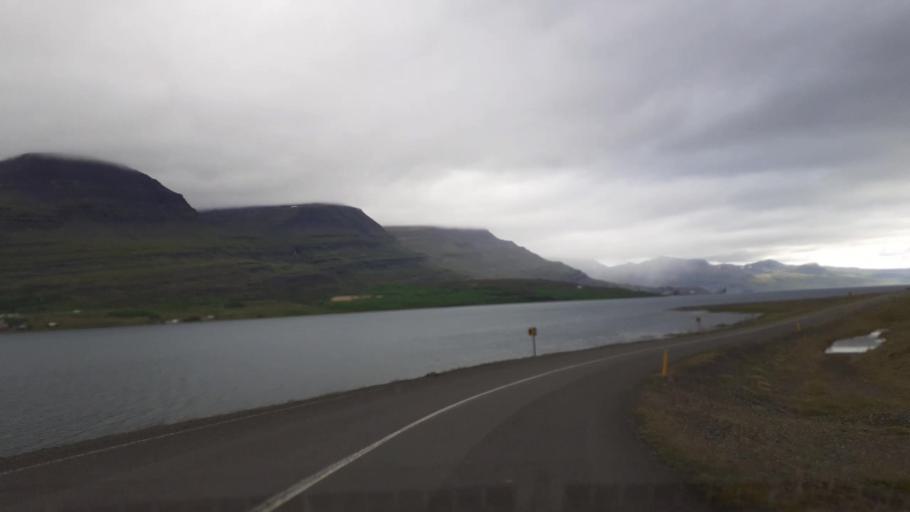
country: IS
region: East
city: Reydarfjoerdur
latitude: 65.0169
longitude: -14.2150
